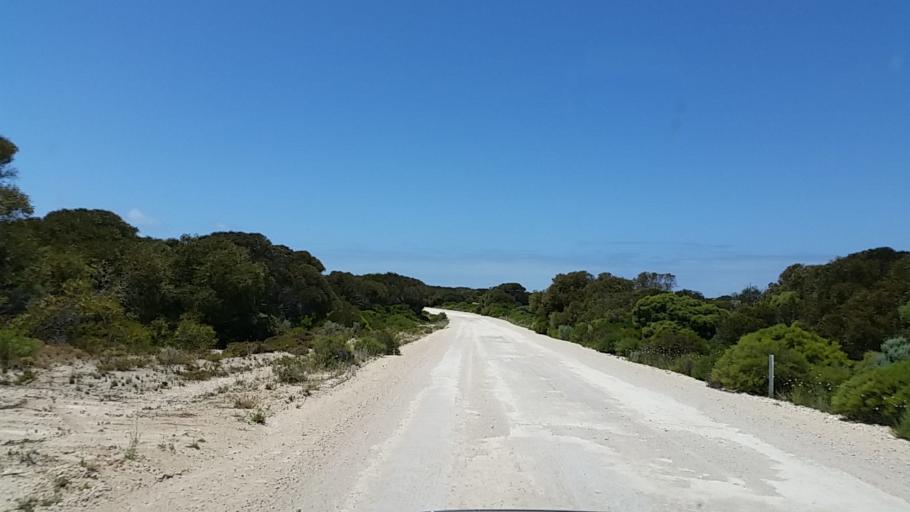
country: AU
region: South Australia
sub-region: Yorke Peninsula
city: Honiton
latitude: -35.2286
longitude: 137.1077
